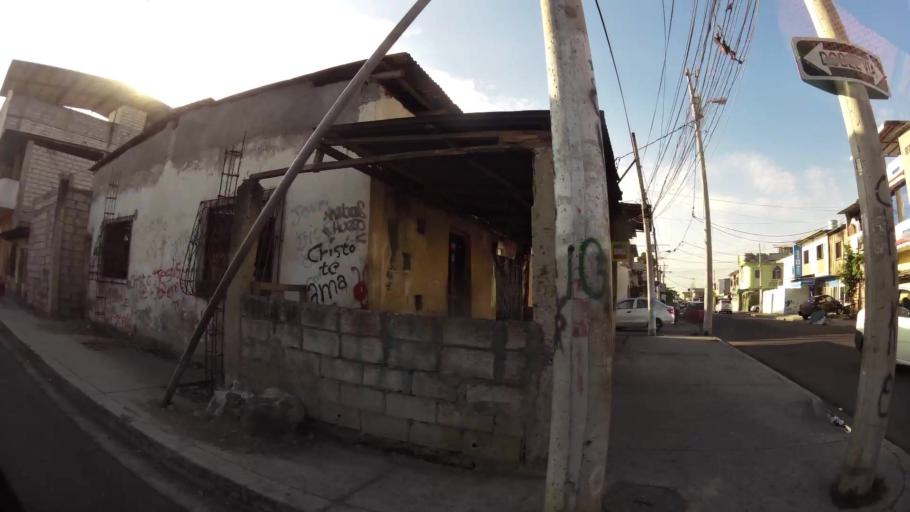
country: EC
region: Guayas
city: Guayaquil
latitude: -2.2277
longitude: -79.9103
